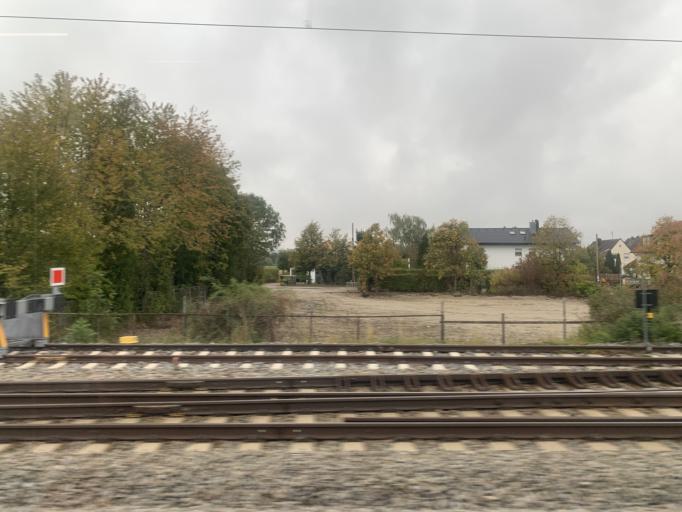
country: DE
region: Bavaria
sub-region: Upper Bavaria
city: Oberschleissheim
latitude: 48.2187
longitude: 11.5416
